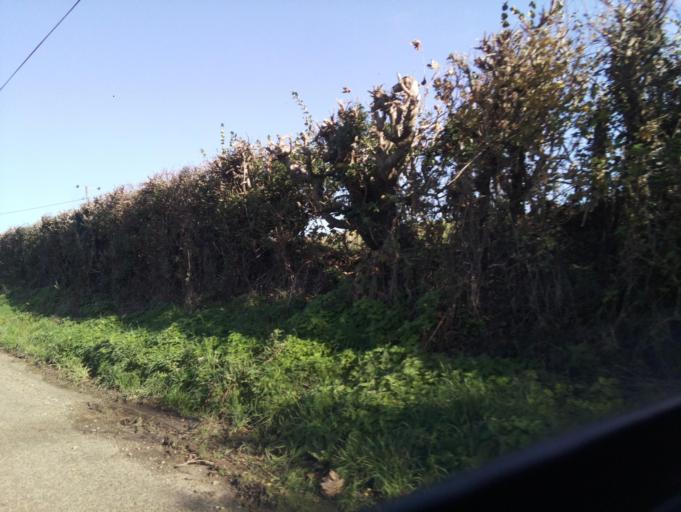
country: GB
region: England
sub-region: Somerset
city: Castle Cary
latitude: 51.0618
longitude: -2.4779
